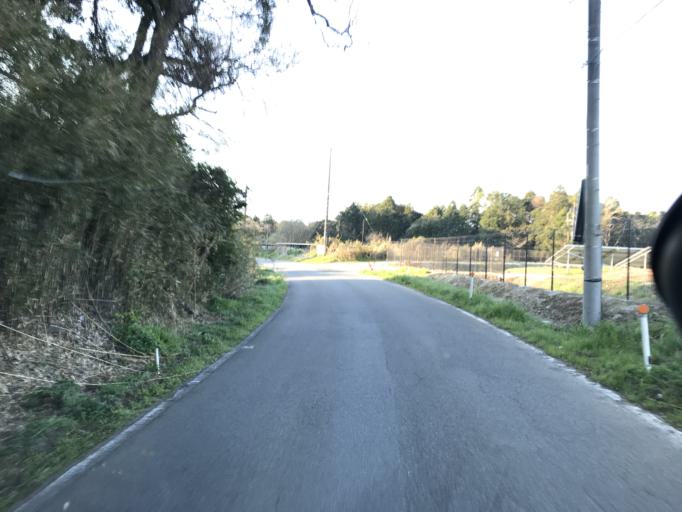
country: JP
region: Chiba
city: Yokaichiba
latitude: 35.7798
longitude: 140.5346
